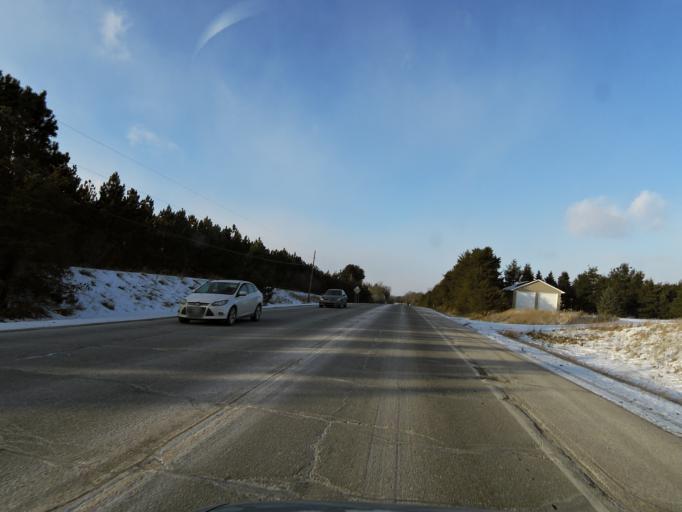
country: US
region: Minnesota
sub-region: Washington County
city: Lake Elmo
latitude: 44.9643
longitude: -92.8831
